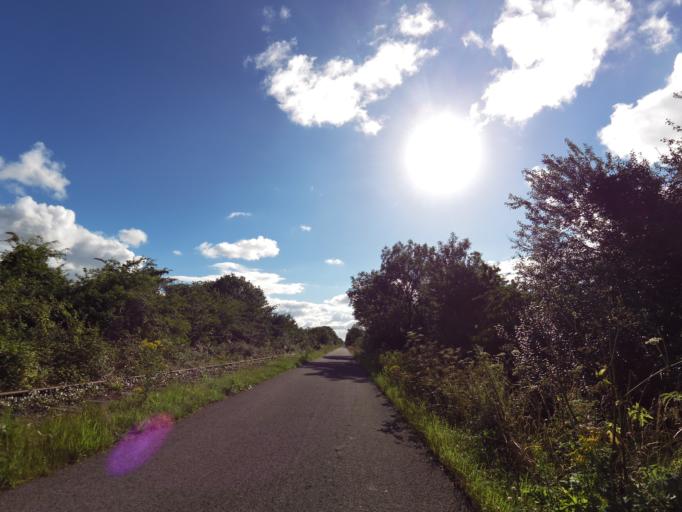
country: IE
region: Leinster
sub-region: Uibh Fhaili
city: Clara
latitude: 53.4208
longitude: -7.6228
